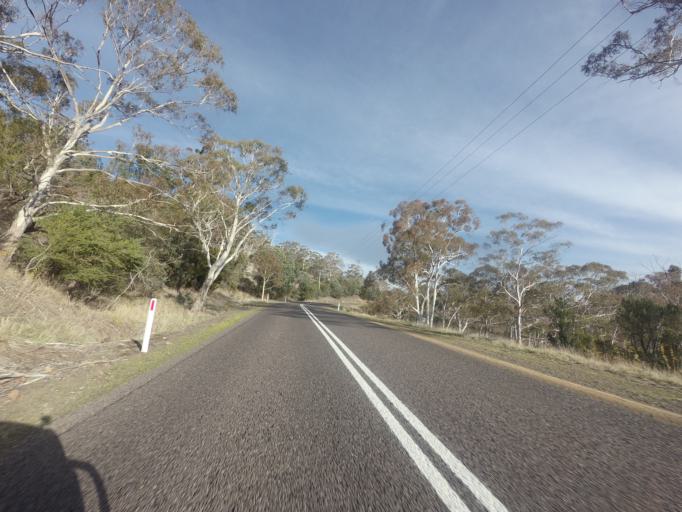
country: AU
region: Tasmania
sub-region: Brighton
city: Bridgewater
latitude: -42.4503
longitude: 147.1544
